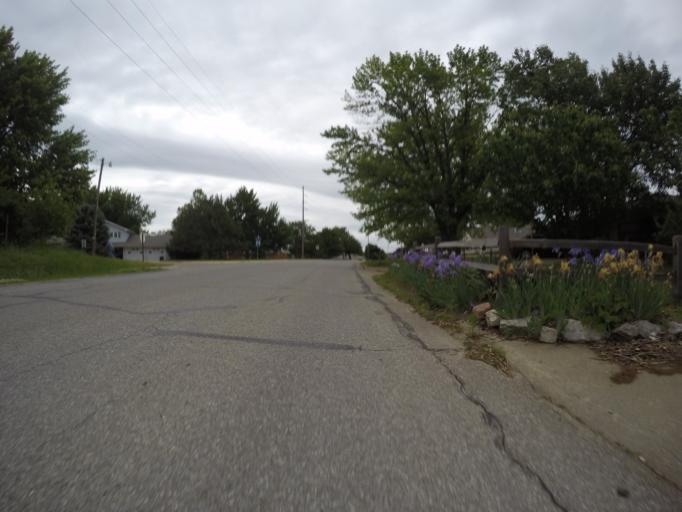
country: US
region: Kansas
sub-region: Pottawatomie County
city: Wamego
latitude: 39.2007
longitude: -96.3165
